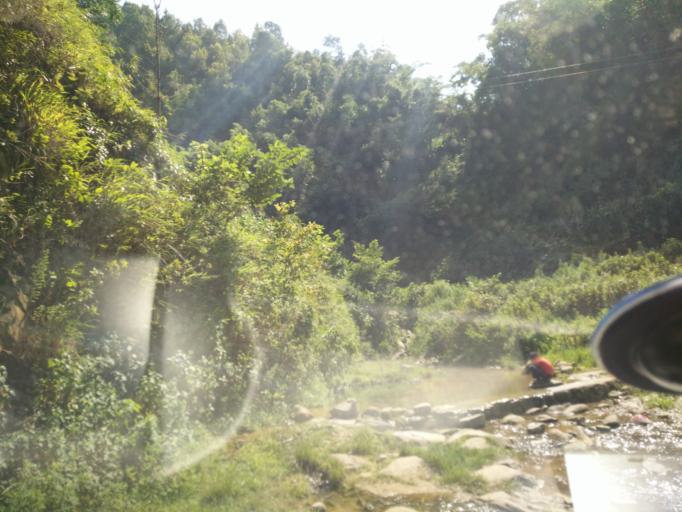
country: CN
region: Guangxi Zhuangzu Zizhiqu
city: Xinzhou
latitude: 25.1848
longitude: 105.6884
